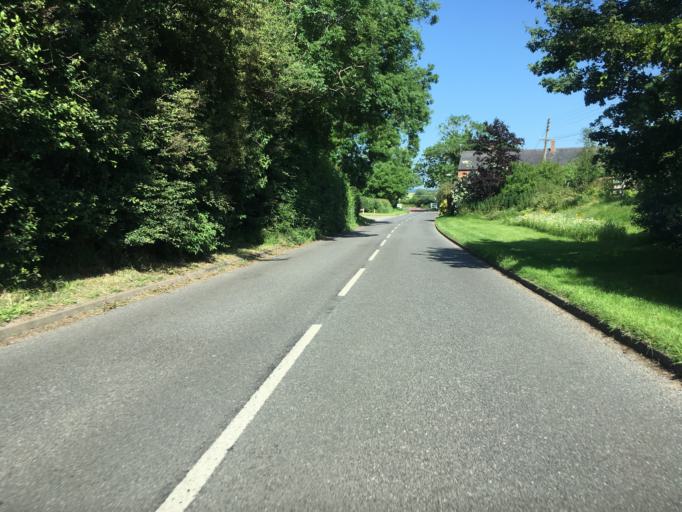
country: GB
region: England
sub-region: Buckinghamshire
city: Newton Longville
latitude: 51.9513
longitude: -0.7713
